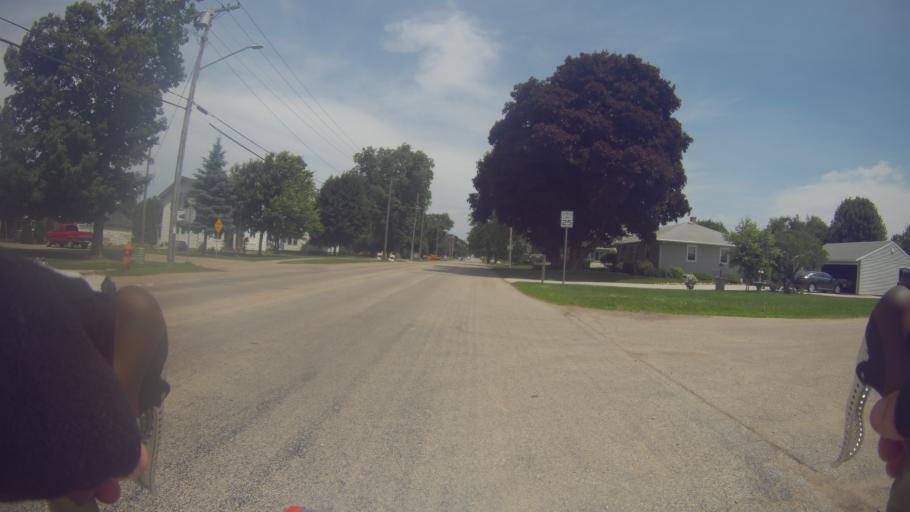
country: US
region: Wisconsin
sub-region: Jefferson County
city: Lake Mills
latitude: 43.0656
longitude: -88.9138
